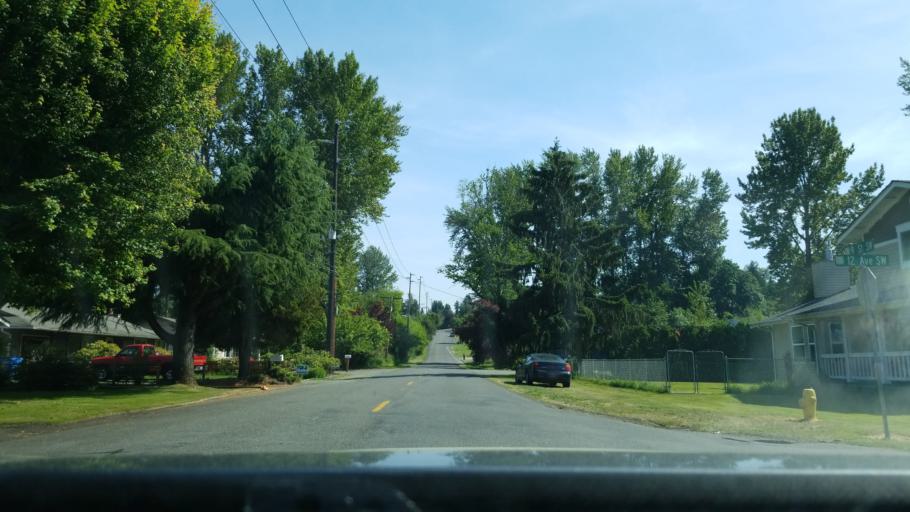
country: US
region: Washington
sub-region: Pierce County
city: Puyallup
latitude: 47.1809
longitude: -122.3054
